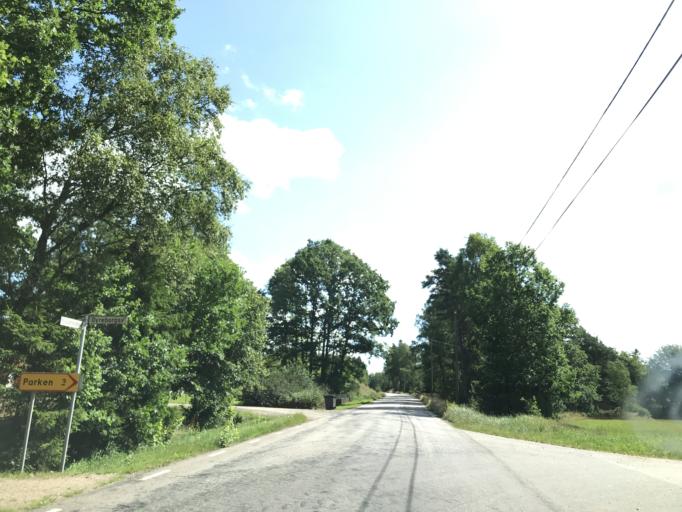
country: SE
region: Halland
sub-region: Laholms Kommun
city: Knared
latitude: 56.5195
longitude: 13.3452
